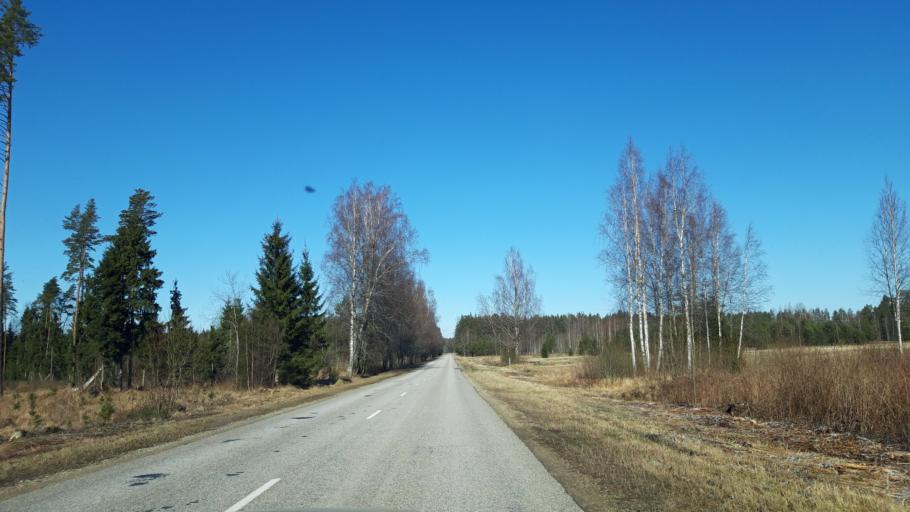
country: LV
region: Strenci
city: Strenci
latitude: 57.6039
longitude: 25.7147
